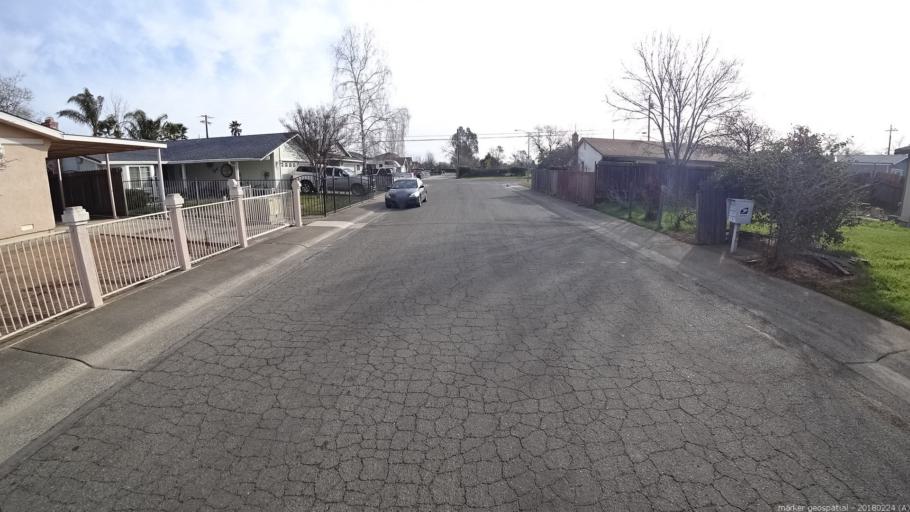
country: US
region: California
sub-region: Sacramento County
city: Rio Linda
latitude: 38.6906
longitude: -121.4622
